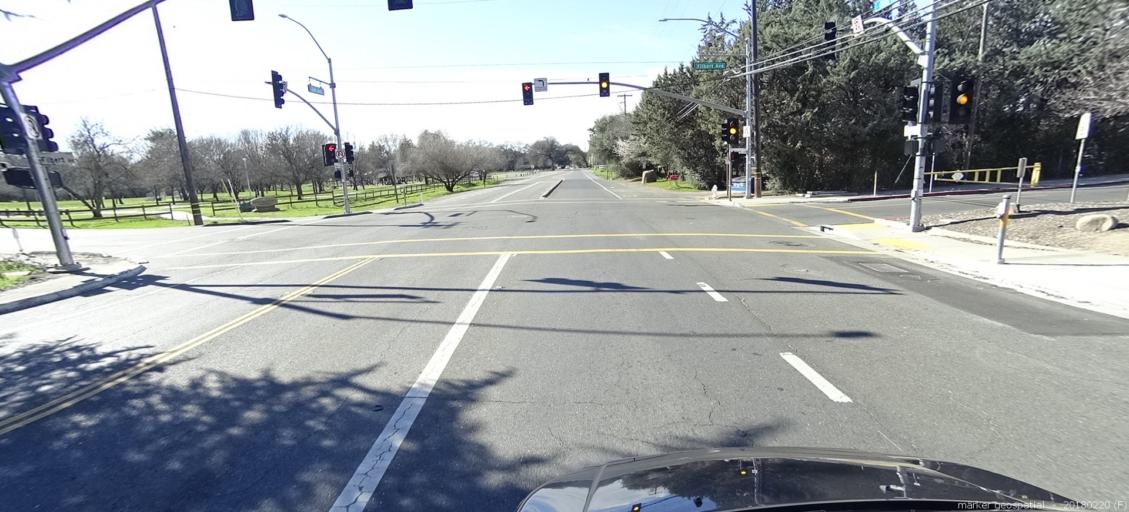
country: US
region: California
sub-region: Sacramento County
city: Orangevale
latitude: 38.7002
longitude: -121.2151
